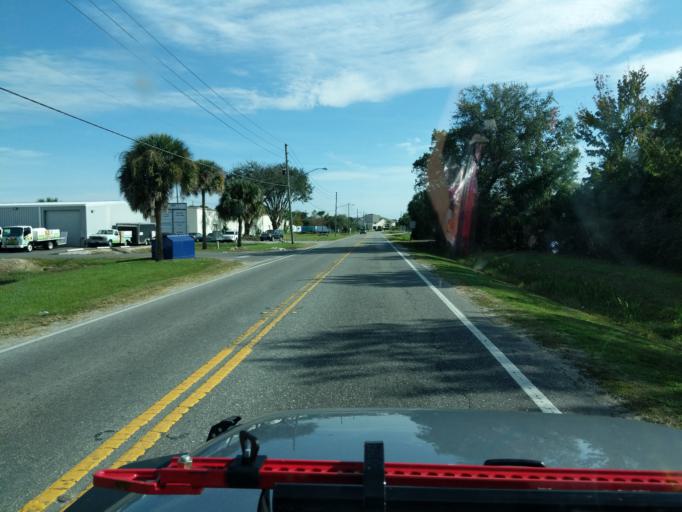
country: US
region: Florida
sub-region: Orange County
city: Ocoee
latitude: 28.5643
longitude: -81.5491
